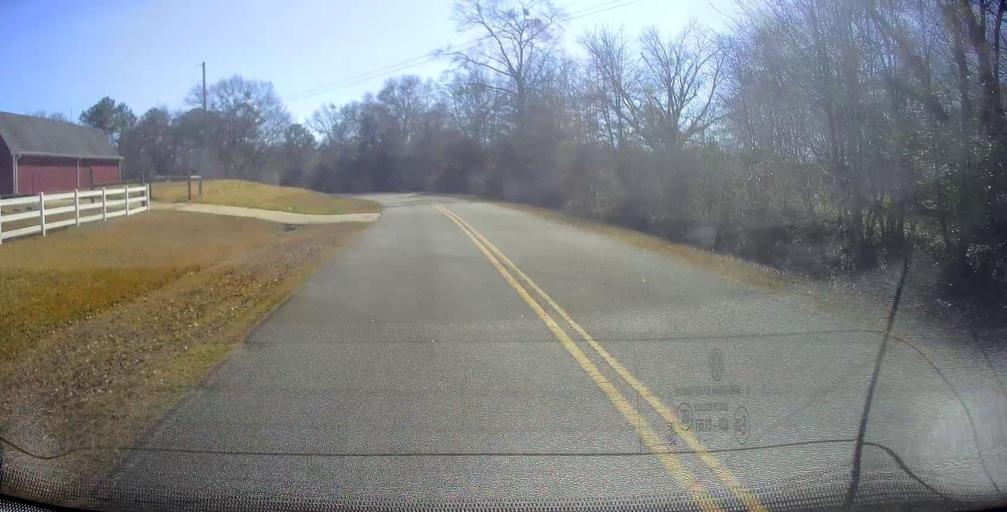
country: US
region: Georgia
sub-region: Peach County
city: Byron
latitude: 32.6229
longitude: -83.8352
